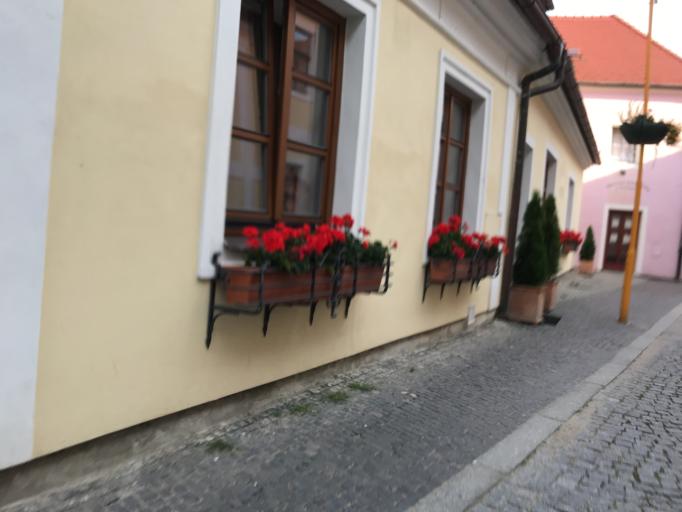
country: CZ
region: Jihocesky
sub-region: Okres Jindrichuv Hradec
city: Trebon
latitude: 49.0035
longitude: 14.7723
